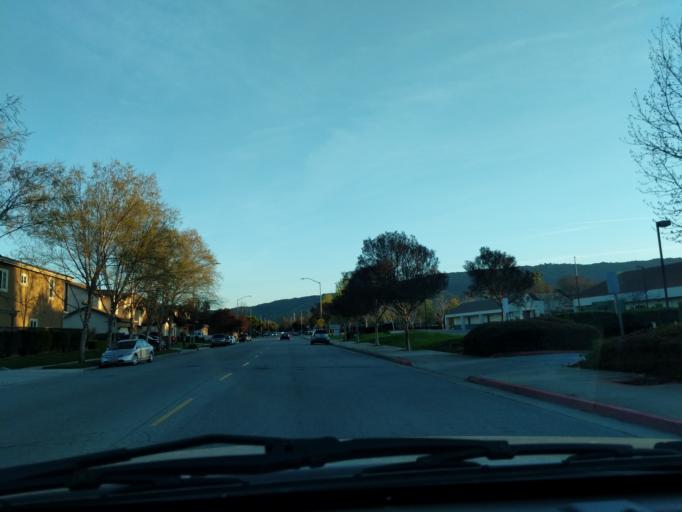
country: US
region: California
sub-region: Santa Clara County
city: Gilroy
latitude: 37.0215
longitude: -121.5916
